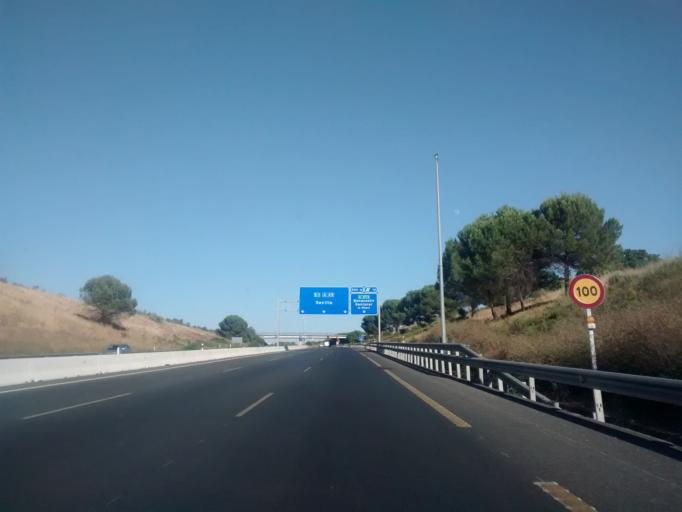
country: ES
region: Andalusia
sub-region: Provincia de Sevilla
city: Benacazon
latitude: 37.3637
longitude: -6.2100
